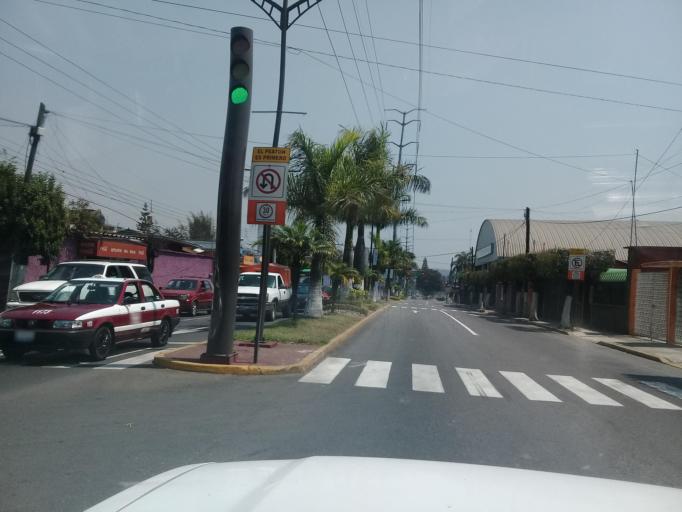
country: MX
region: Veracruz
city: Ixtac Zoquitlan
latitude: 18.8603
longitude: -97.0633
